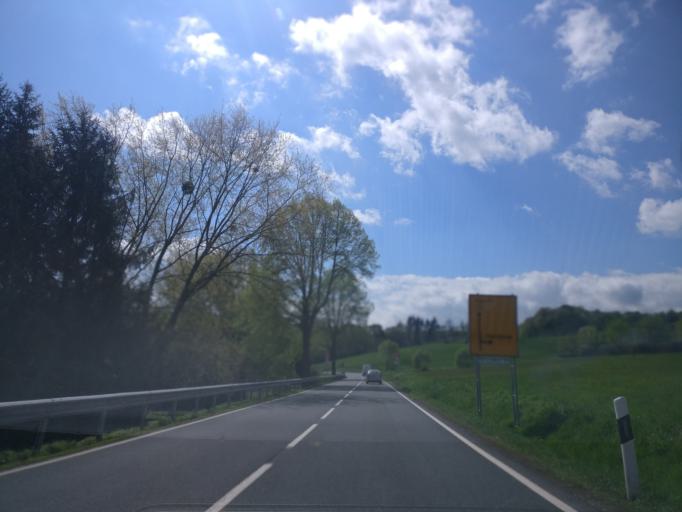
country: DE
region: Lower Saxony
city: Scheden
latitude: 51.4526
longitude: 9.7063
